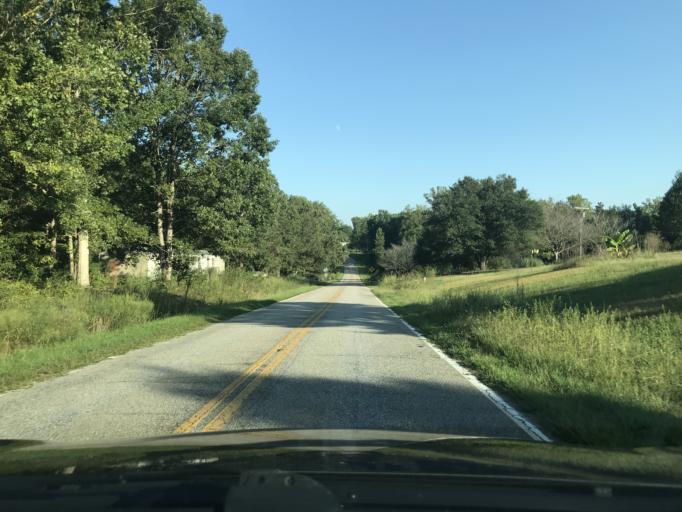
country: US
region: South Carolina
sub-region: Spartanburg County
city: Mayo
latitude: 35.1060
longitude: -81.7769
